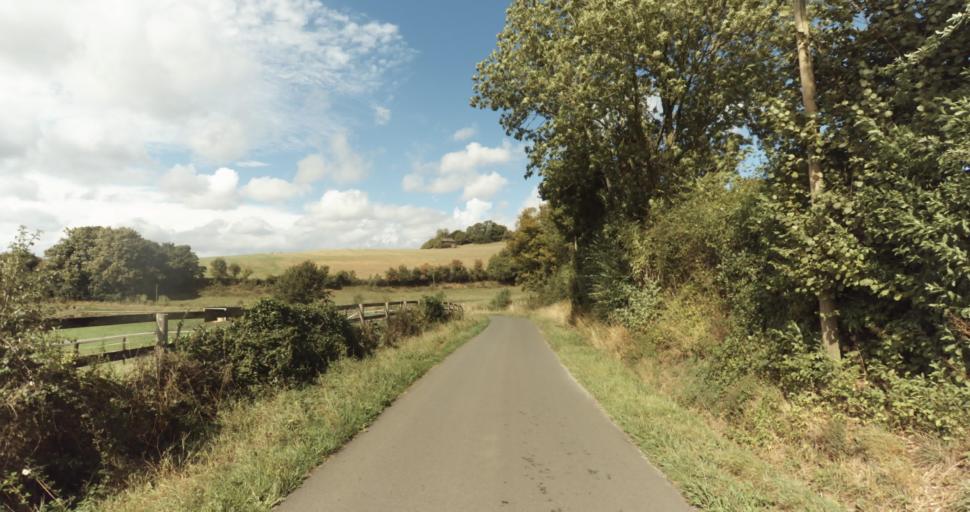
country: FR
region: Lower Normandy
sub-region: Departement de l'Orne
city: Gace
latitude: 48.7814
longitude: 0.3059
